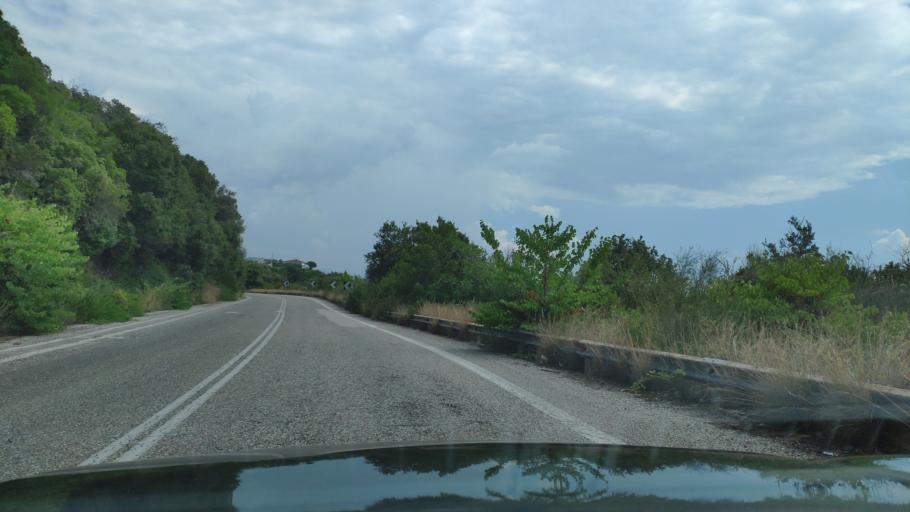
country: GR
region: West Greece
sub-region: Nomos Aitolias kai Akarnanias
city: Menidi
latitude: 39.0015
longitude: 21.1486
